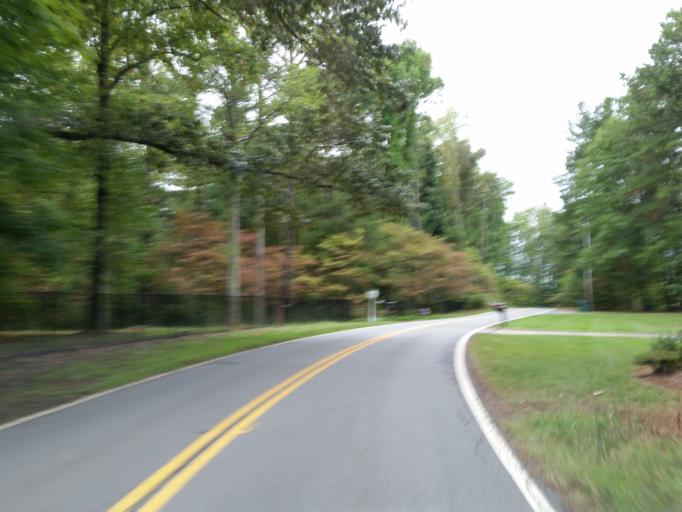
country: US
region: Georgia
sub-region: Cherokee County
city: Woodstock
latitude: 34.0807
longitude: -84.4696
